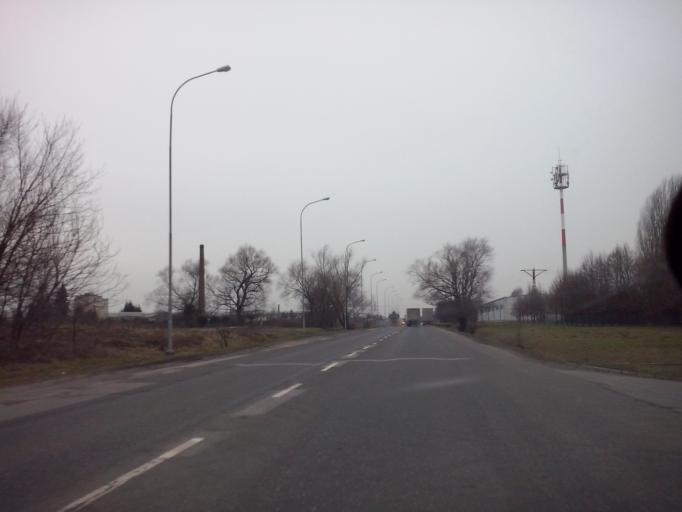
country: PL
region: Lublin Voivodeship
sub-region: Zamosc
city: Zamosc
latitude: 50.7355
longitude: 23.2409
